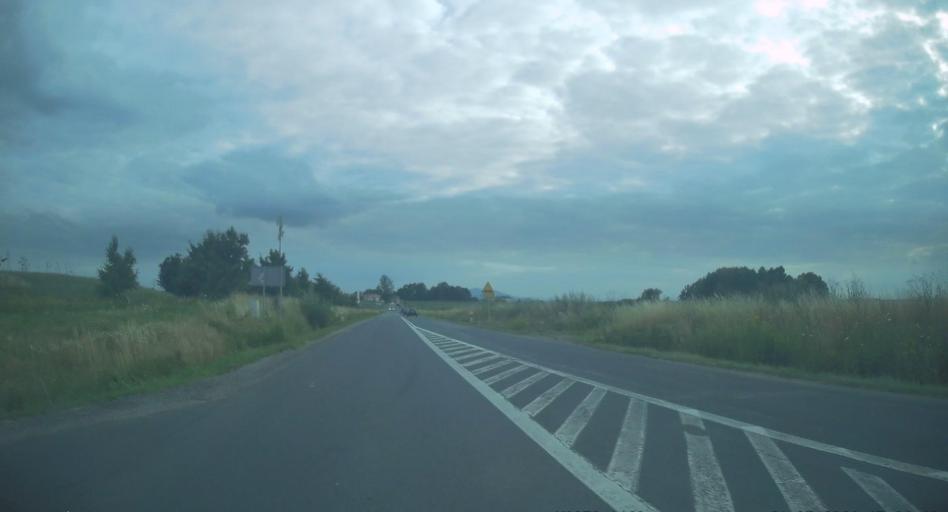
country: PL
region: Lower Silesian Voivodeship
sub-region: Powiat wroclawski
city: Tyniec Maly
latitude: 51.0176
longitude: 16.8764
